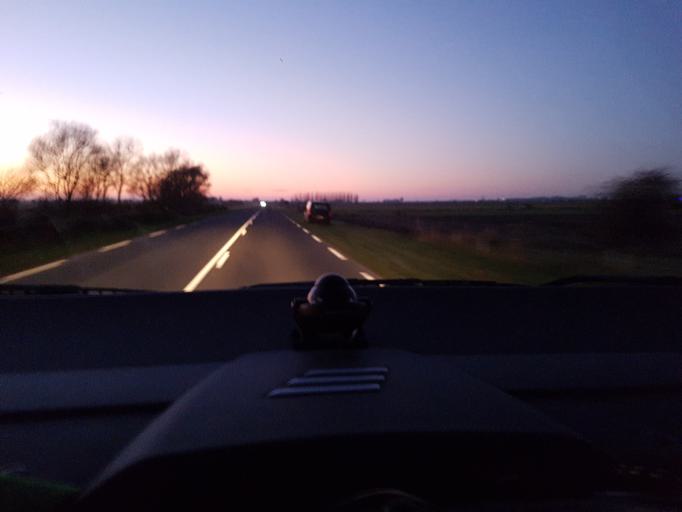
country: FR
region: Picardie
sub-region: Departement de la Somme
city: Pende
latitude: 50.1858
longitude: 1.5788
